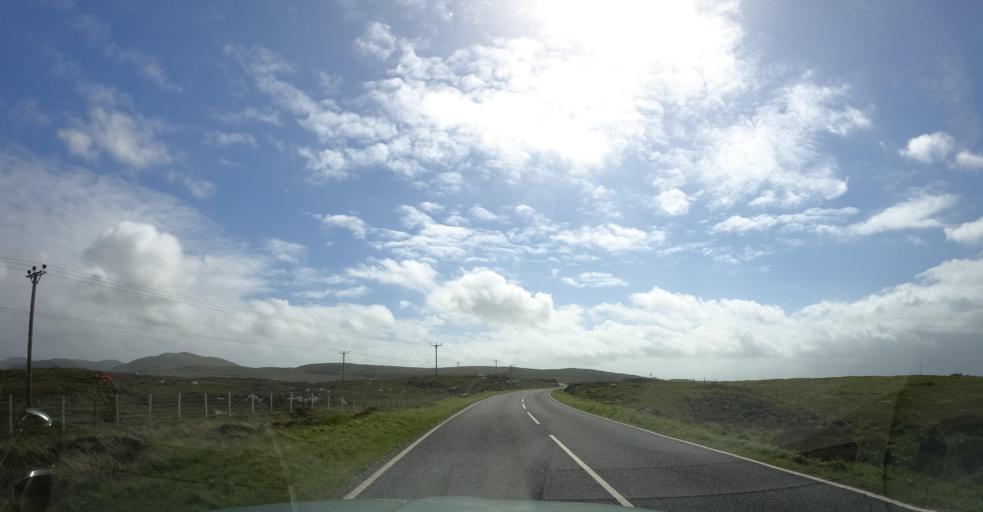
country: GB
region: Scotland
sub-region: Eilean Siar
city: Isle of South Uist
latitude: 57.2451
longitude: -7.3824
